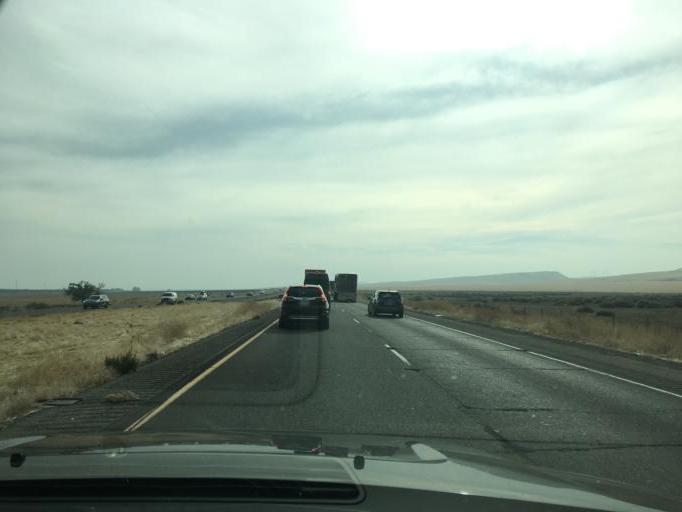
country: US
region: California
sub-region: Fresno County
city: Coalinga
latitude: 36.3521
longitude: -120.3196
